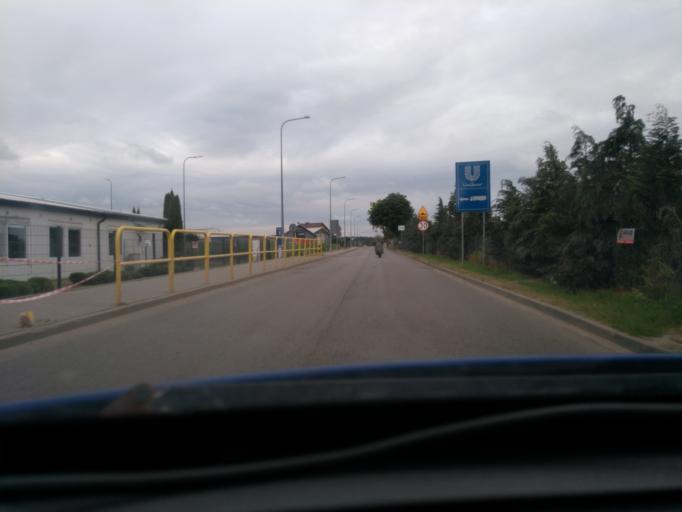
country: PL
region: Pomeranian Voivodeship
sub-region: Powiat kartuski
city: Banino
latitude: 54.3863
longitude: 18.4059
